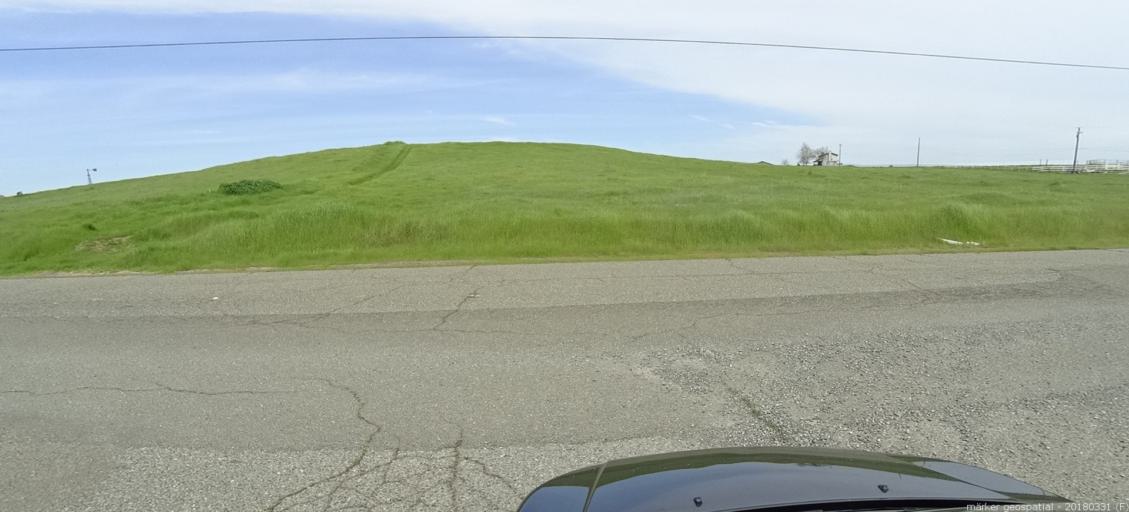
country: US
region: California
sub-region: Sacramento County
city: Rancho Murieta
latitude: 38.4897
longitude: -121.1345
